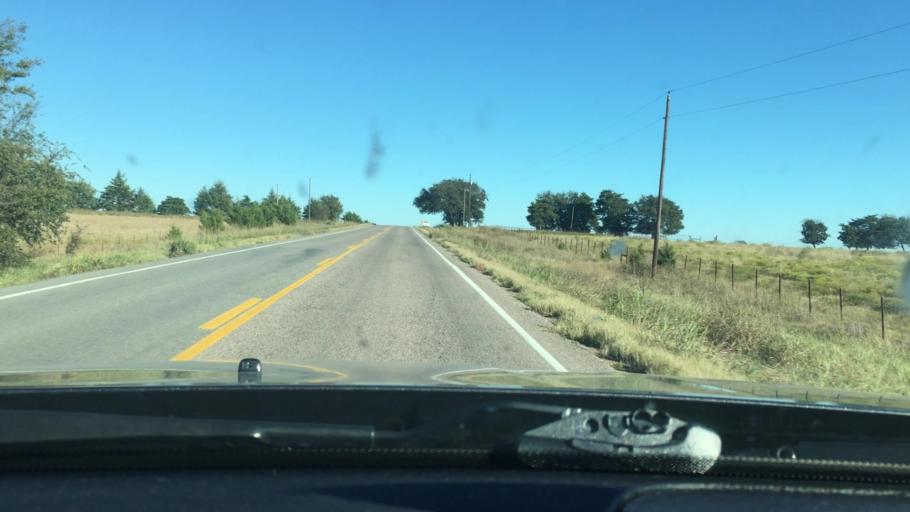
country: US
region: Oklahoma
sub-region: Johnston County
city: Tishomingo
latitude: 34.1566
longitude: -96.7058
